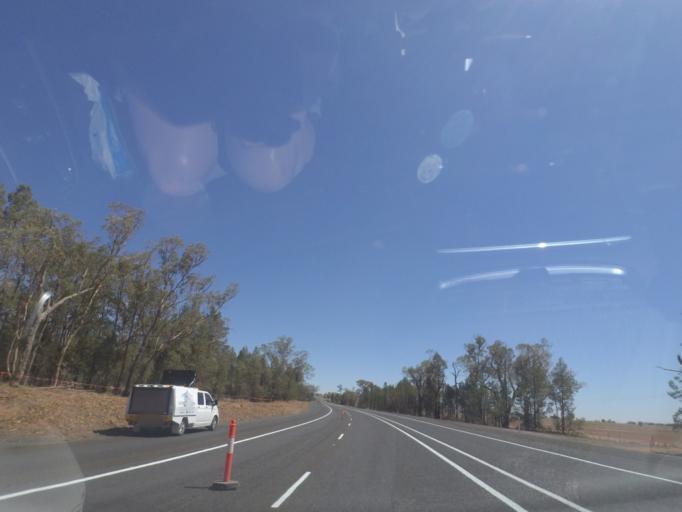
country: AU
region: New South Wales
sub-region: Gilgandra
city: Gilgandra
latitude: -31.6647
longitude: 148.7191
